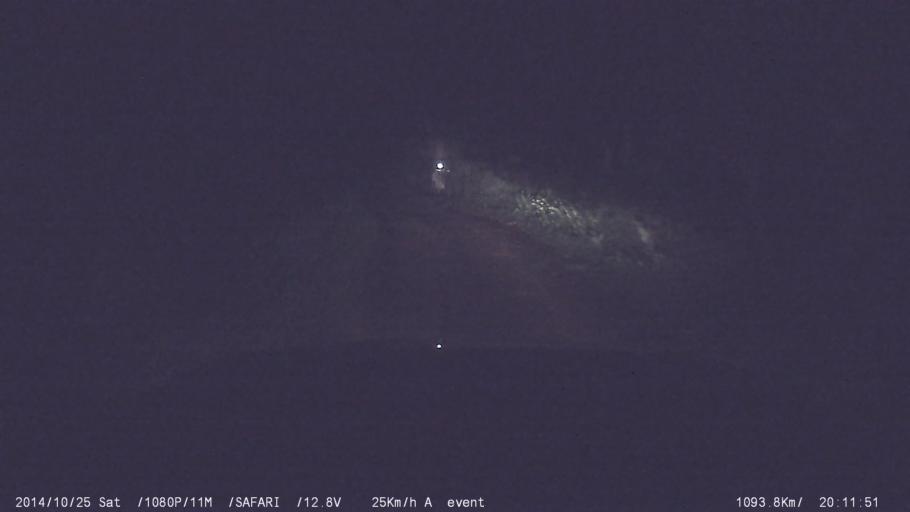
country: IN
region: Kerala
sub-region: Kottayam
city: Palackattumala
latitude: 9.7831
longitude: 76.5610
